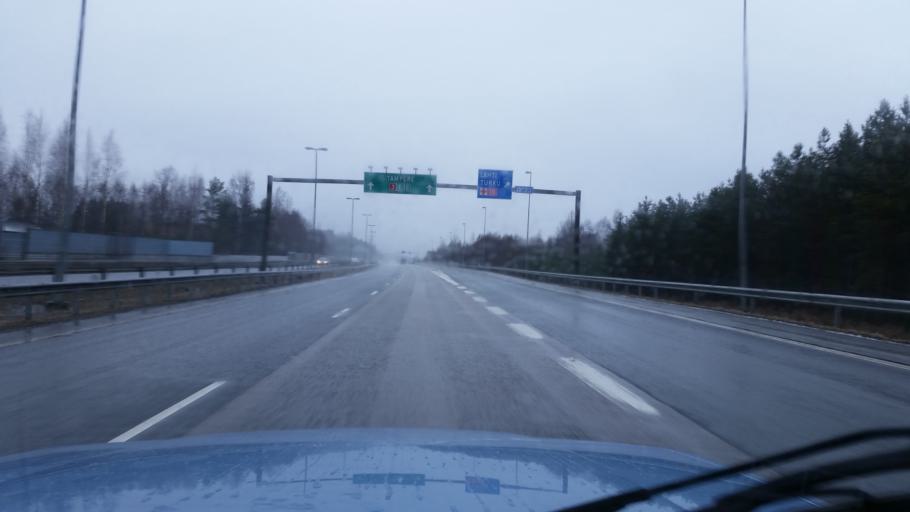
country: FI
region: Haeme
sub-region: Haemeenlinna
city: Haemeenlinna
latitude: 60.9642
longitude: 24.4796
